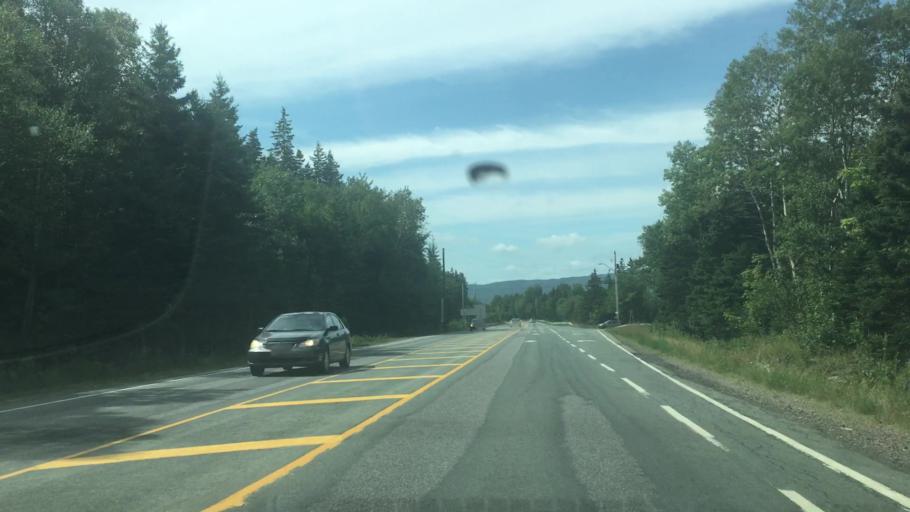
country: CA
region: Nova Scotia
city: Sydney Mines
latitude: 46.2386
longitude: -60.5636
